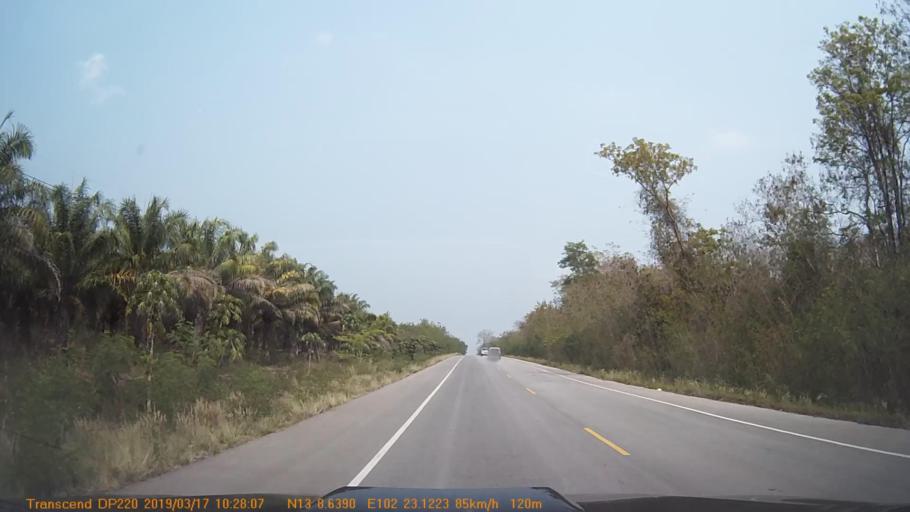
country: TH
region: Chanthaburi
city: Soi Dao
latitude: 13.1442
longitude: 102.3852
